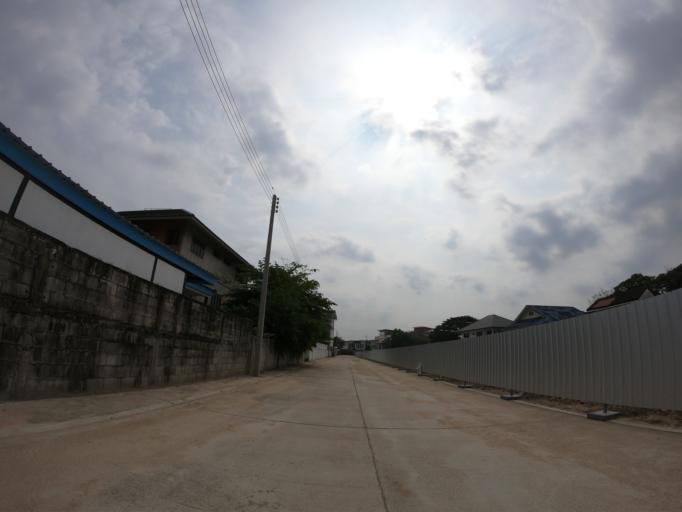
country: TH
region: Chiang Mai
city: Chiang Mai
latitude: 18.7661
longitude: 98.9792
